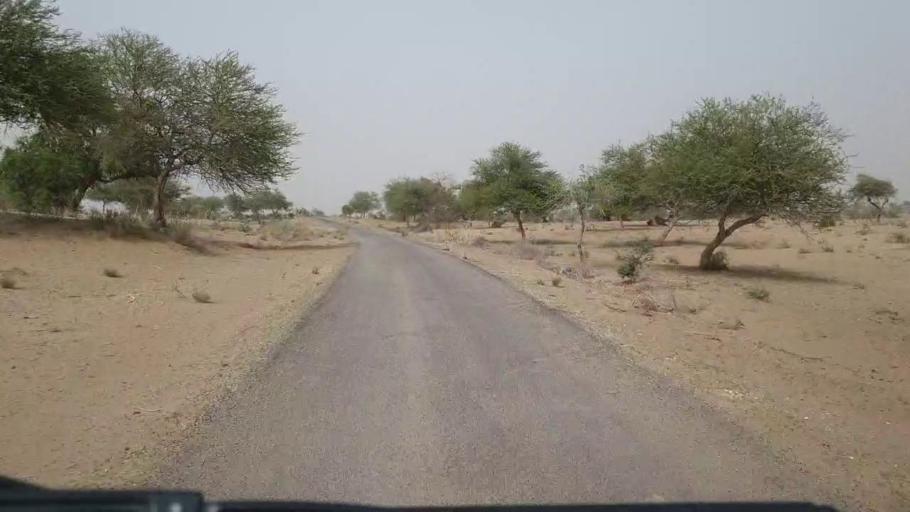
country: PK
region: Sindh
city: Islamkot
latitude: 25.3732
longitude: 70.5325
